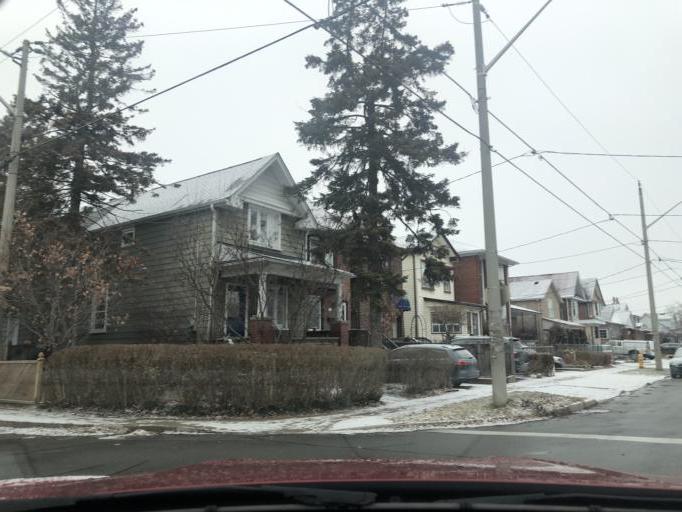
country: CA
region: Ontario
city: Toronto
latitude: 43.6842
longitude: -79.3435
